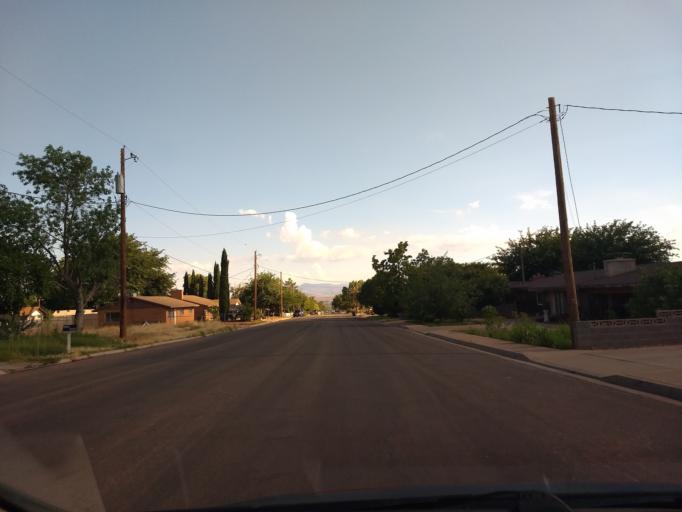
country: US
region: Utah
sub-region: Washington County
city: Washington
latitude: 37.1353
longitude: -113.5082
